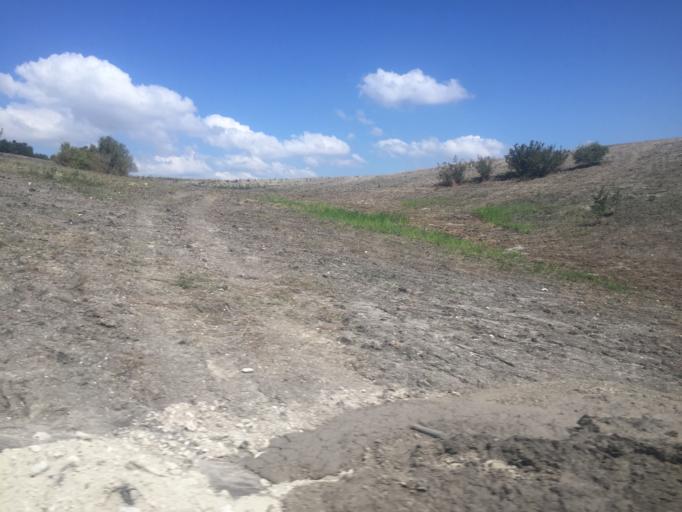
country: TR
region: Balikesir
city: Gobel
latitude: 39.9683
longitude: 28.1602
